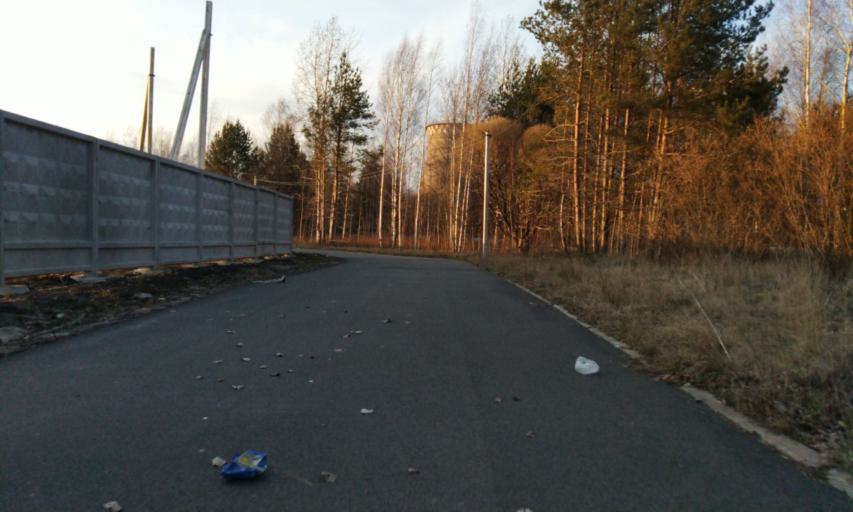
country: RU
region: Leningrad
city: Novoye Devyatkino
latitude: 60.0753
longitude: 30.4690
